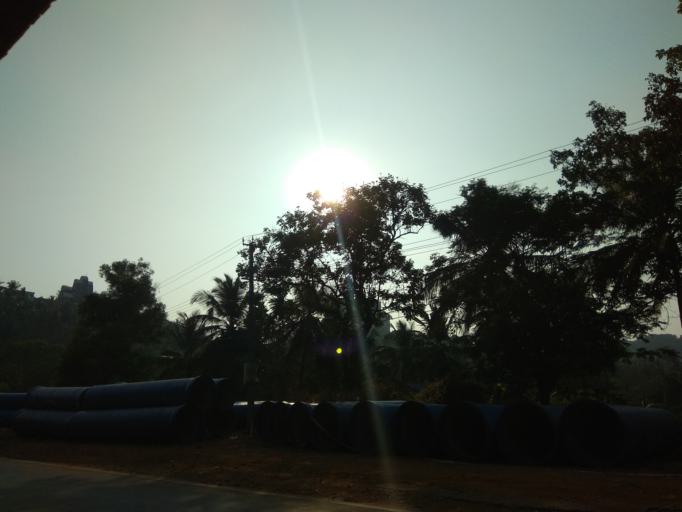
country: IN
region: Karnataka
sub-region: Dakshina Kannada
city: Mangalore
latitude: 12.9117
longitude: 74.8547
